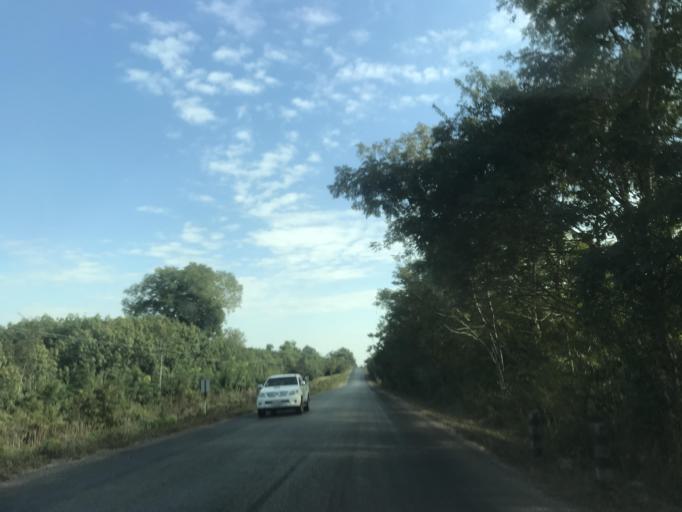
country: LA
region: Khammouan
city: Muang Hinboun
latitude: 17.8110
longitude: 104.4712
